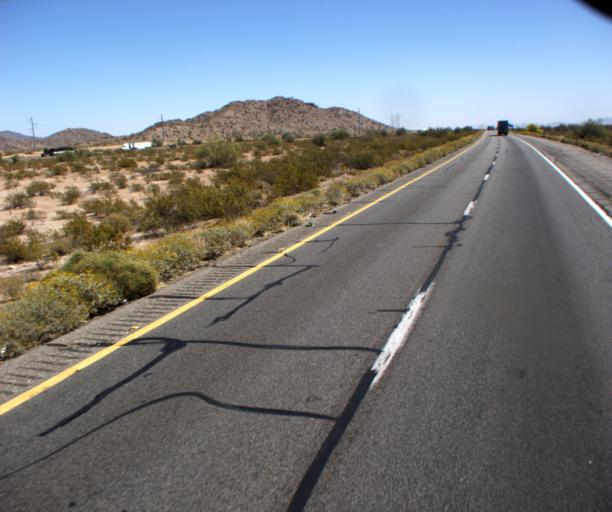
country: US
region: Arizona
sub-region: Maricopa County
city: Buckeye
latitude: 33.4311
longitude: -112.6451
